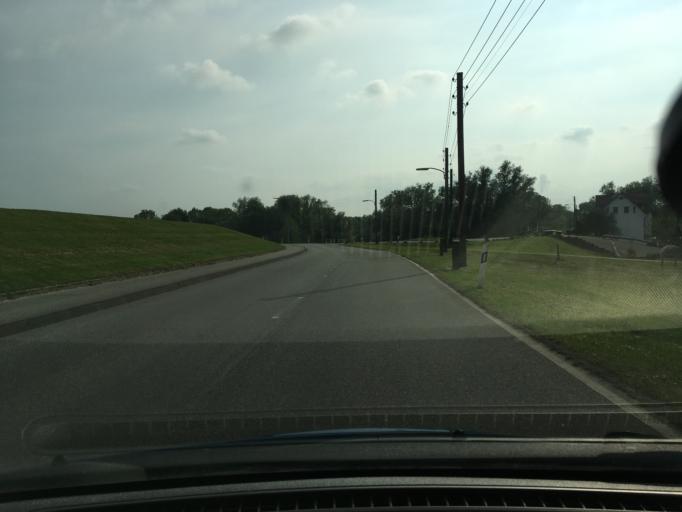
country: DE
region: Hamburg
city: Rothenburgsort
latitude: 53.5046
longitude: 10.0528
